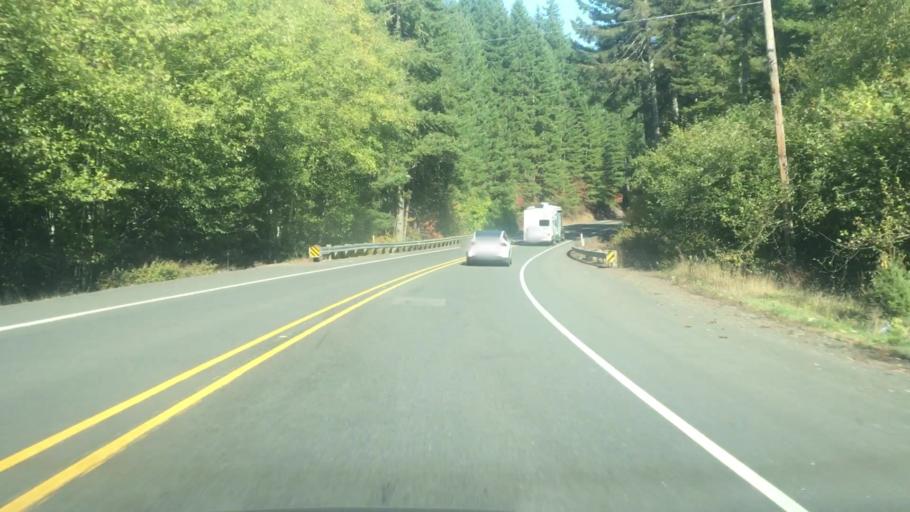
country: US
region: Oregon
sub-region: Polk County
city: Grand Ronde
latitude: 45.0687
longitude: -123.7283
